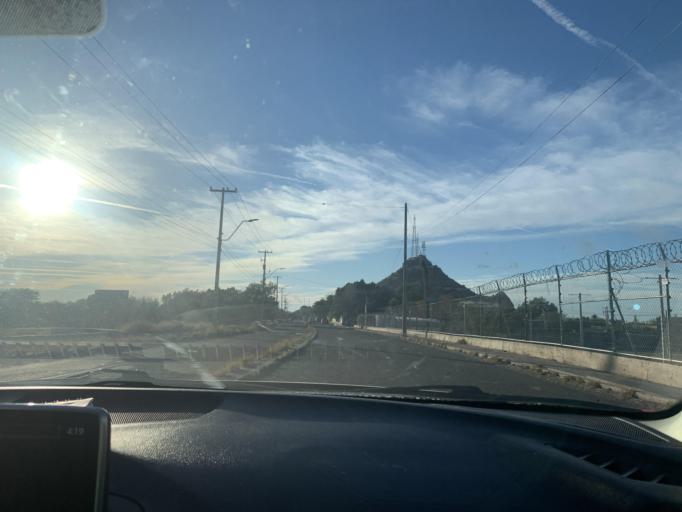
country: MX
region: Sonora
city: Hermosillo
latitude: 29.0725
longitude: -110.9380
